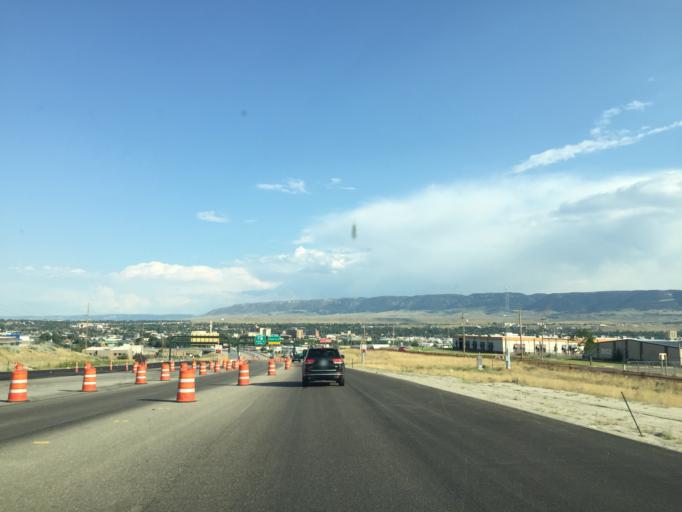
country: US
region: Wyoming
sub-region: Natrona County
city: Casper
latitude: 42.8626
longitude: -106.3410
